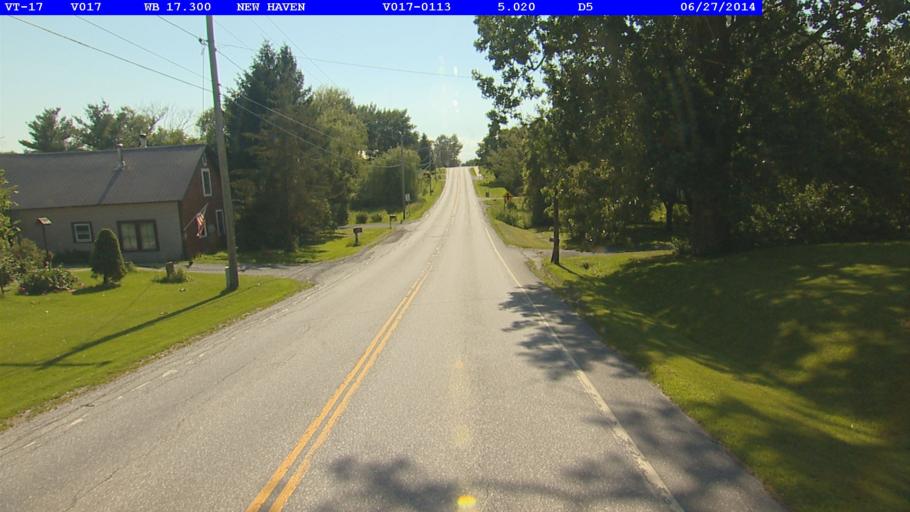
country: US
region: Vermont
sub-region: Addison County
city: Bristol
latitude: 44.1246
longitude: -73.1506
